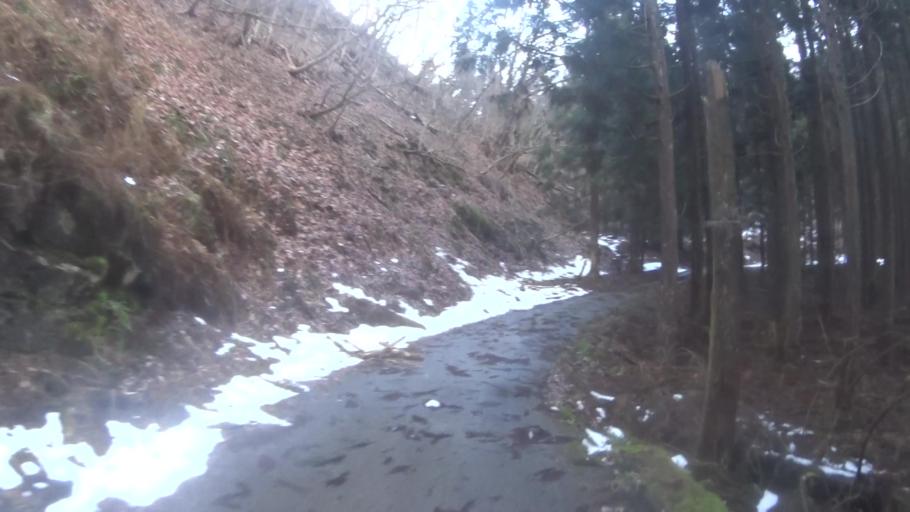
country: JP
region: Kyoto
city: Maizuru
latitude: 35.4027
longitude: 135.5019
